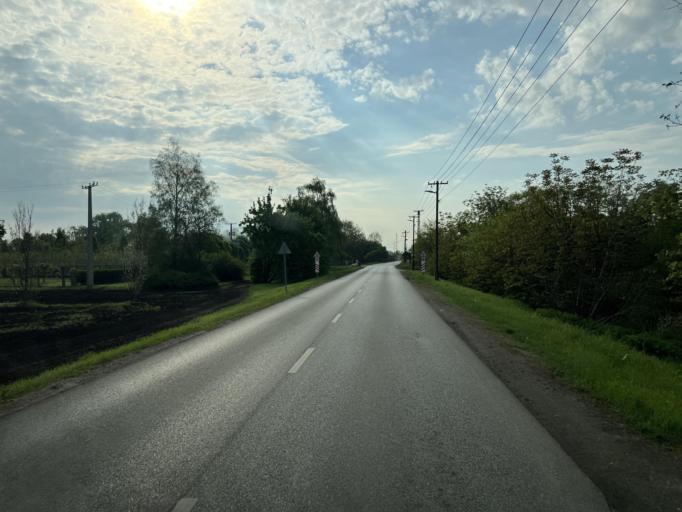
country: HU
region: Pest
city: Cegledbercel
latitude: 47.2090
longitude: 19.7325
